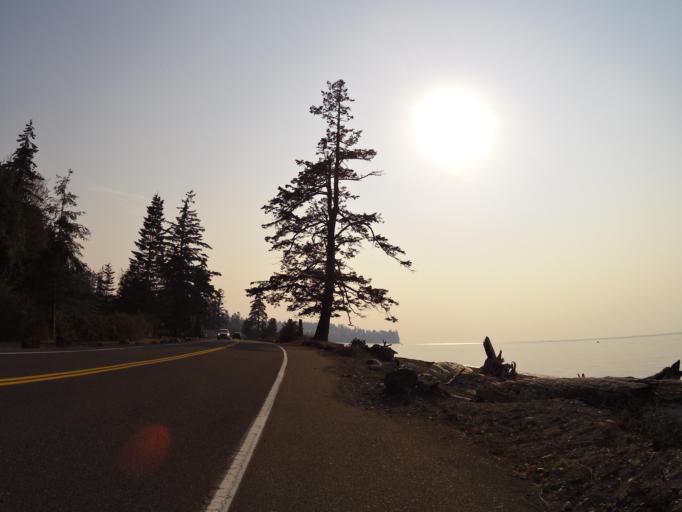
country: US
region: Washington
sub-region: Whatcom County
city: Birch Bay
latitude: 48.9044
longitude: -122.7702
